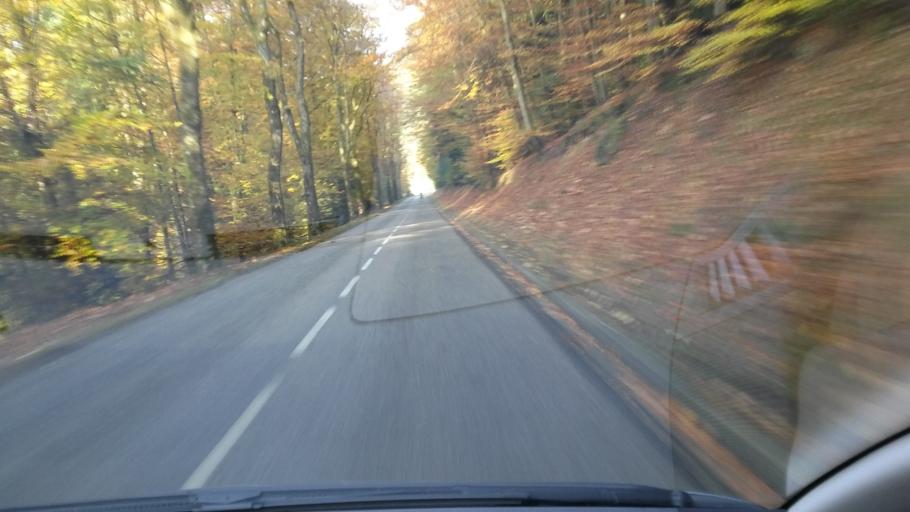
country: FR
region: Lorraine
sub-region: Departement de la Moselle
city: Dabo
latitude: 48.7003
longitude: 7.2117
